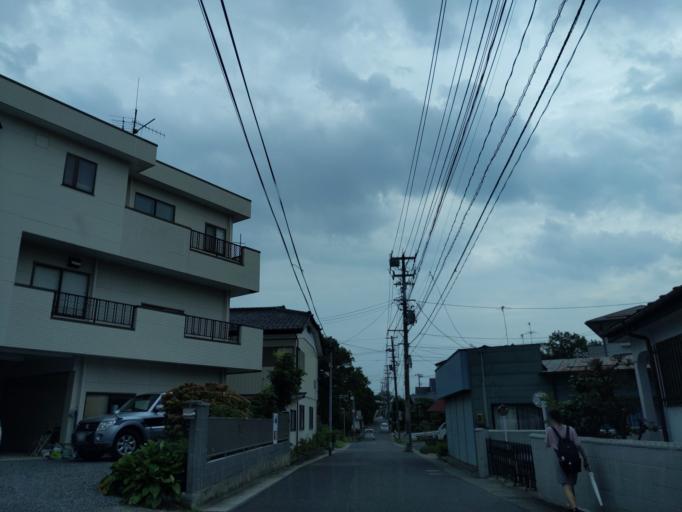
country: JP
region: Fukushima
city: Koriyama
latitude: 37.3818
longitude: 140.3565
